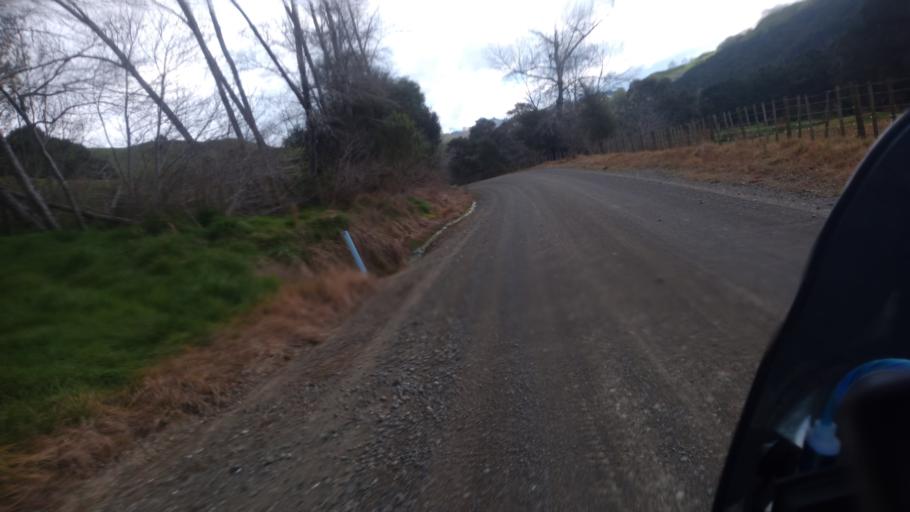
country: NZ
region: Gisborne
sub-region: Gisborne District
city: Gisborne
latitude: -38.2032
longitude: 178.2435
